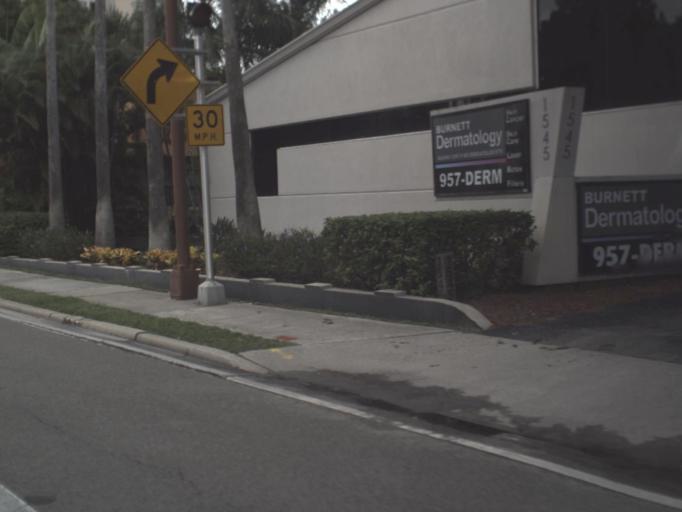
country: US
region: Florida
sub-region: Sarasota County
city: Sarasota
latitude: 27.3286
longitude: -82.5389
